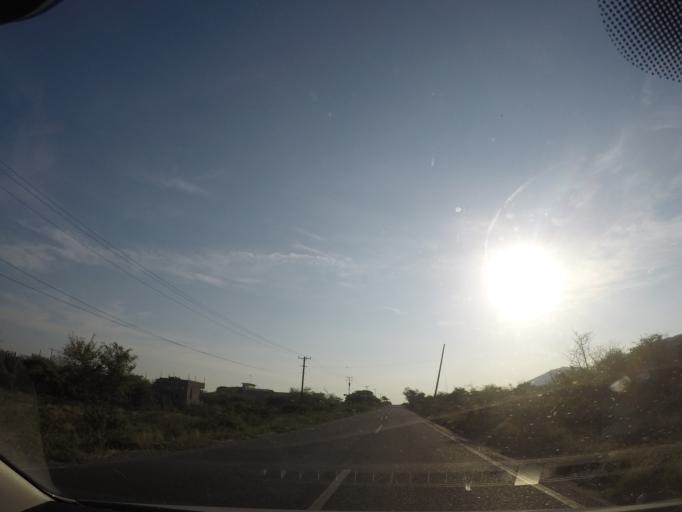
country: MX
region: Oaxaca
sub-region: Santo Domingo Tehuantepec
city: La Noria
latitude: 16.2319
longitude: -95.1763
